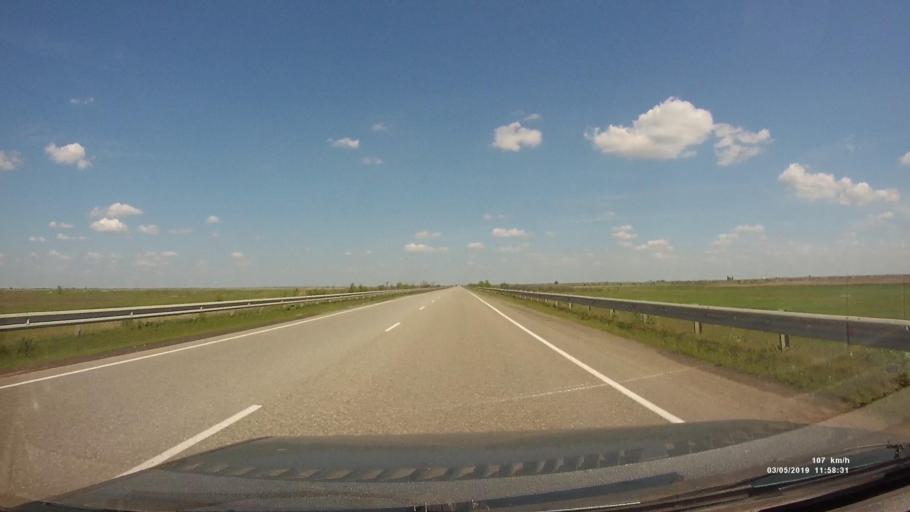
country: RU
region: Rostov
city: Bagayevskaya
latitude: 47.2216
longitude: 40.3204
